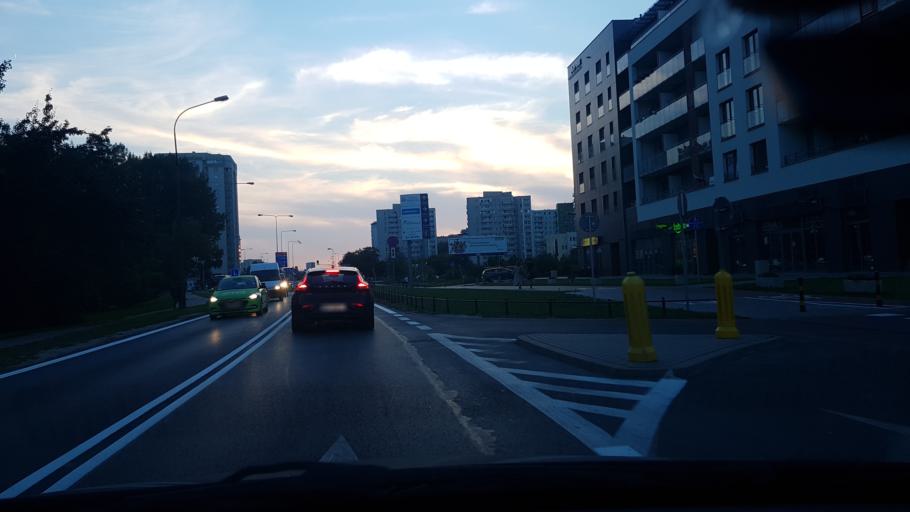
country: PL
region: Masovian Voivodeship
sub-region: Warszawa
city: Targowek
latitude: 52.2924
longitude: 21.0551
